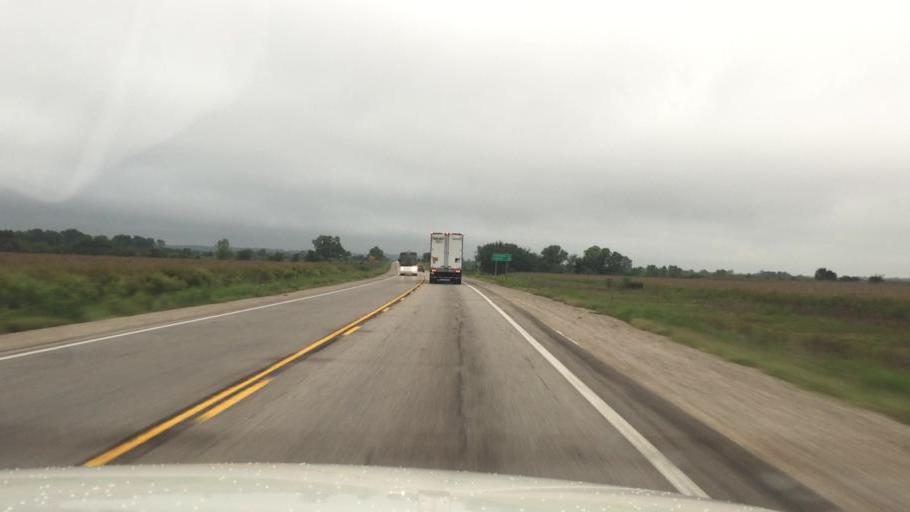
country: US
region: Kansas
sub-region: Montgomery County
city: Cherryvale
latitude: 37.2052
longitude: -95.5847
